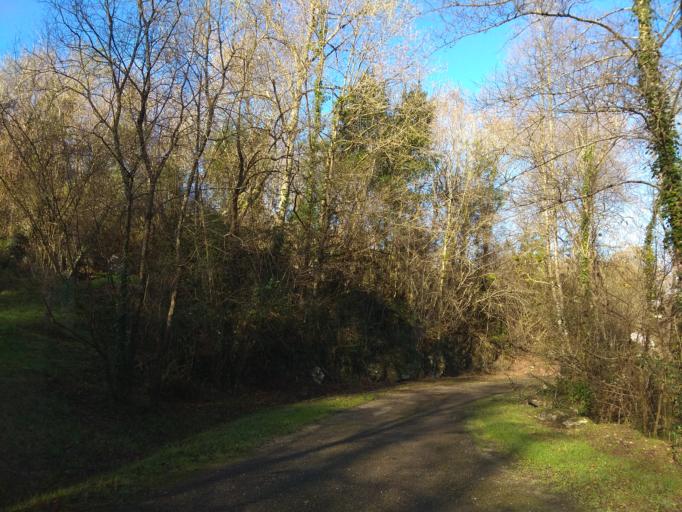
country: ES
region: Cantabria
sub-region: Provincia de Cantabria
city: Entrambasaguas
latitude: 43.3653
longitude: -3.6604
